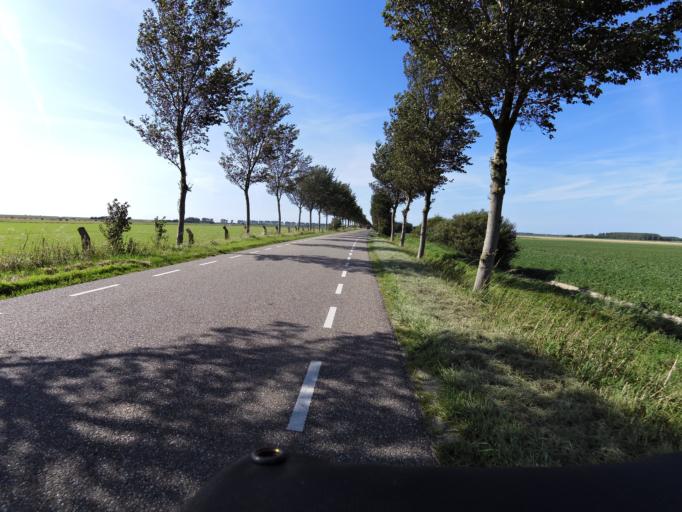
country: NL
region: South Holland
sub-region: Gemeente Goeree-Overflakkee
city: Dirksland
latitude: 51.7213
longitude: 4.0837
